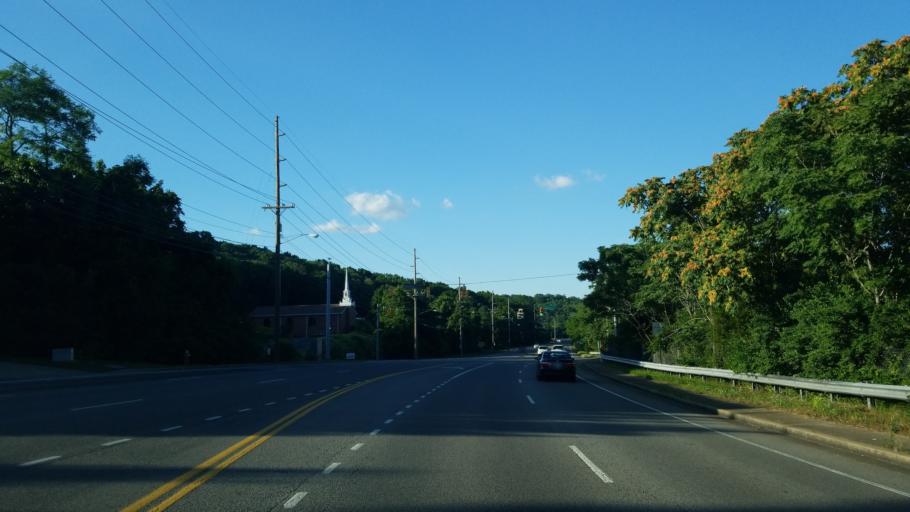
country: US
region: Tennessee
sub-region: Williamson County
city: Brentwood
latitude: 36.0387
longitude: -86.7861
